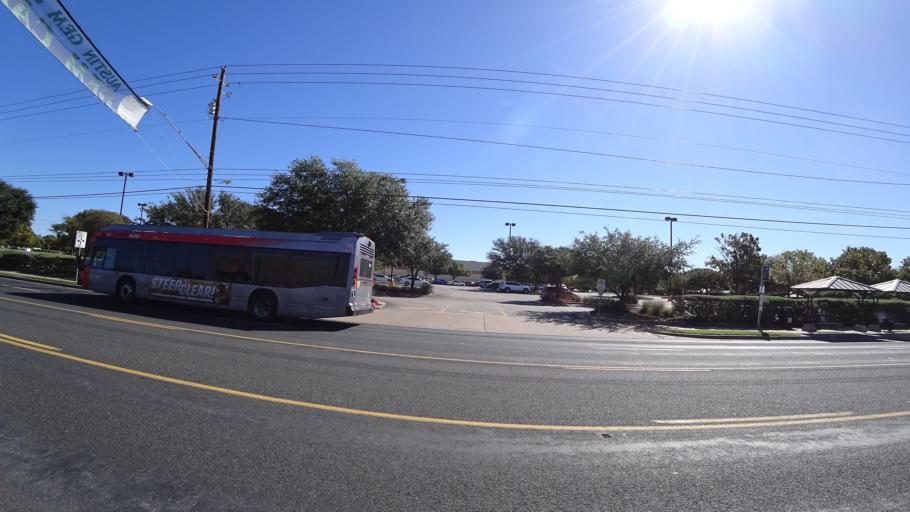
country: US
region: Texas
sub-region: Travis County
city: Rollingwood
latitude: 30.2301
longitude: -97.8010
